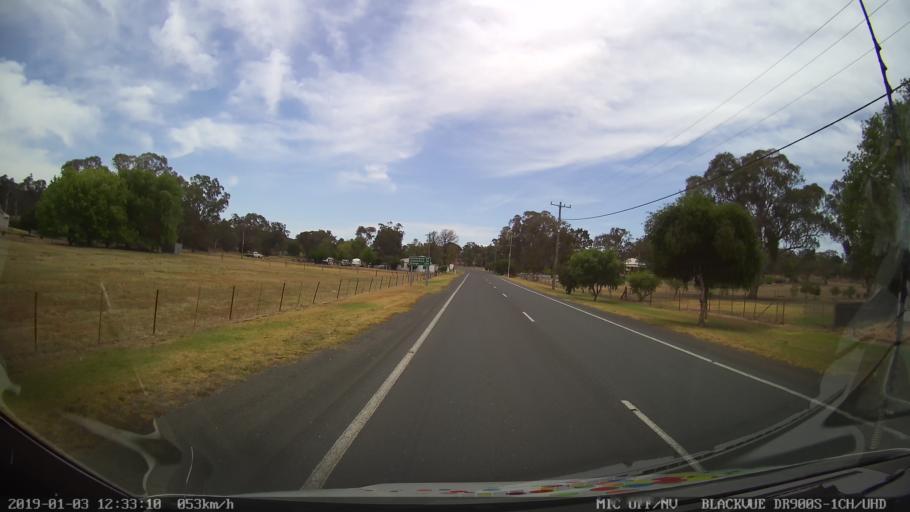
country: AU
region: New South Wales
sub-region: Weddin
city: Grenfell
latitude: -33.8873
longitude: 148.1626
